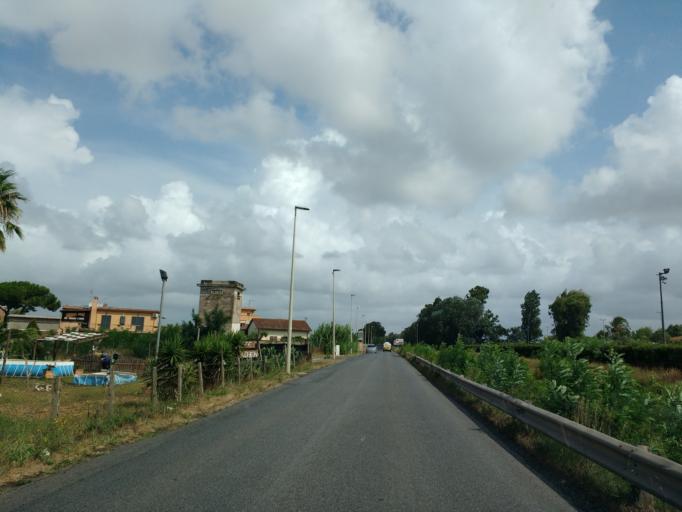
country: IT
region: Latium
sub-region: Citta metropolitana di Roma Capitale
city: Acilia-Castel Fusano-Ostia Antica
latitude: 41.7526
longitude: 12.3301
